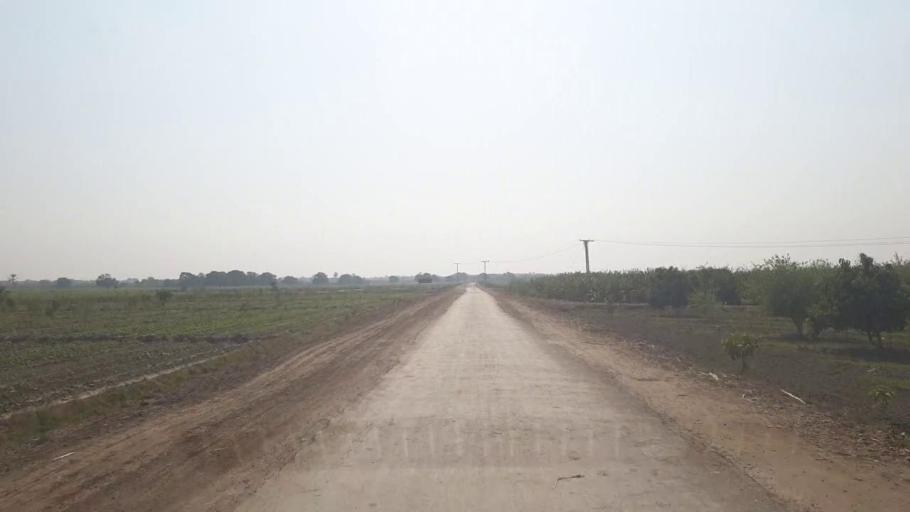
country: PK
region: Sindh
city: Tando Allahyar
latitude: 25.4611
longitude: 68.8149
